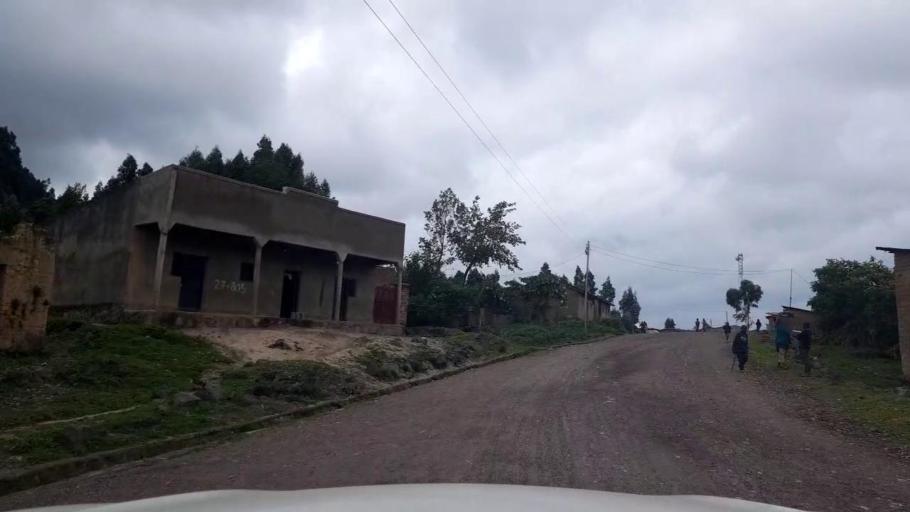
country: RW
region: Northern Province
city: Musanze
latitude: -1.5911
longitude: 29.4673
